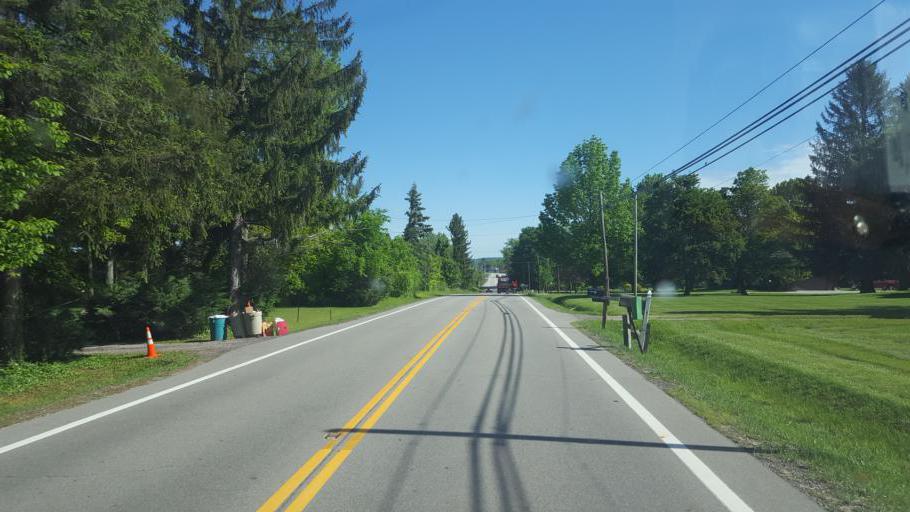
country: US
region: Ohio
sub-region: Summit County
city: Montrose-Ghent
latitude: 41.1309
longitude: -81.7351
